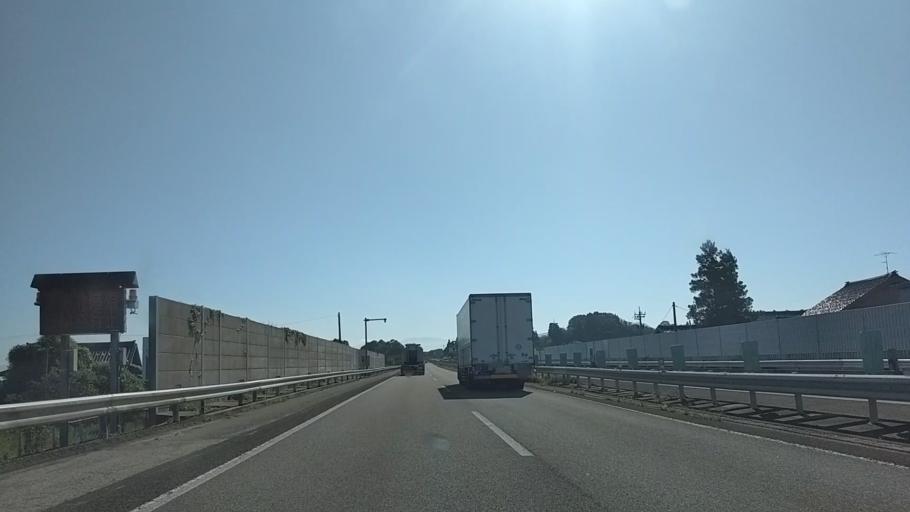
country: JP
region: Toyama
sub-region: Oyabe Shi
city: Oyabe
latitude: 36.6291
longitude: 136.8576
